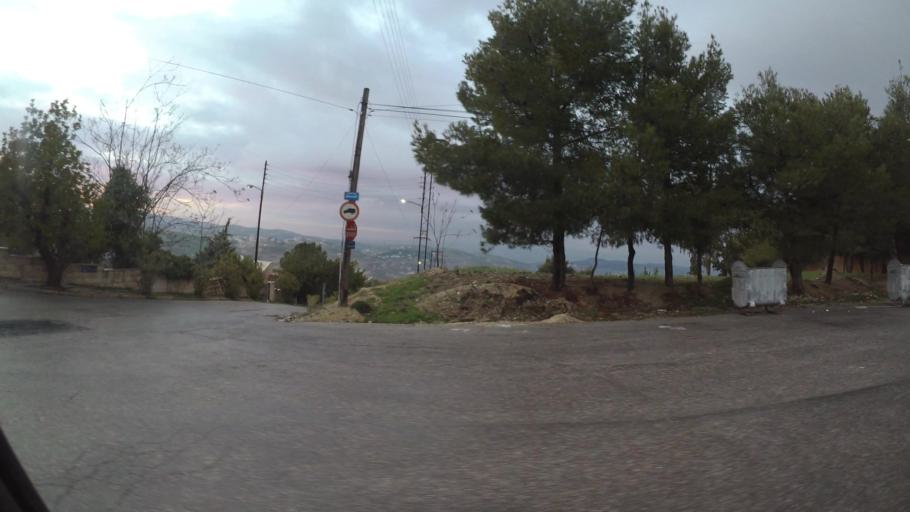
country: JO
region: Amman
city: Al Jubayhah
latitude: 32.0320
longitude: 35.8146
